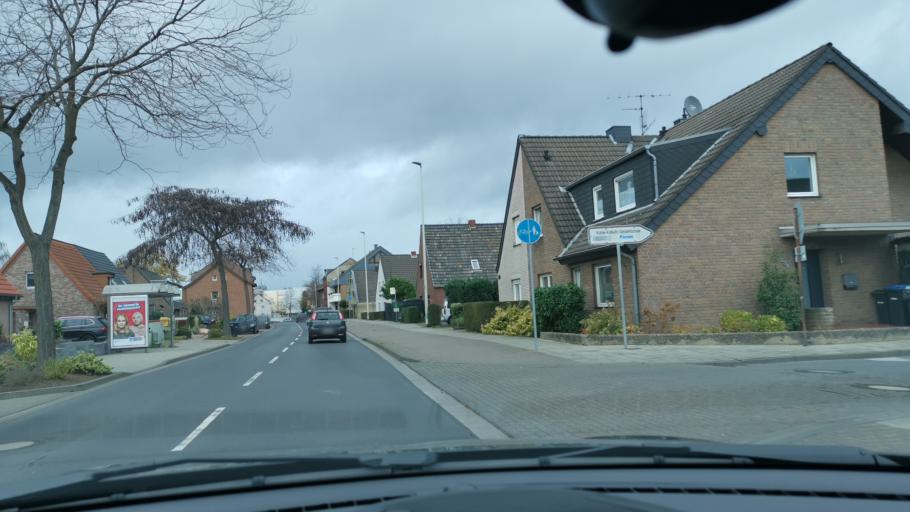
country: DE
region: North Rhine-Westphalia
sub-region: Regierungsbezirk Dusseldorf
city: Grevenbroich
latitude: 51.0812
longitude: 6.5960
